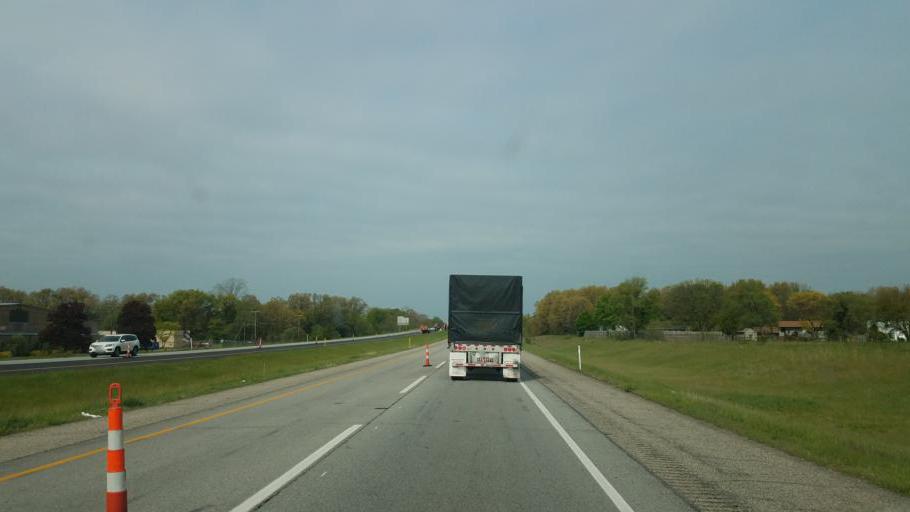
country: US
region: Indiana
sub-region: Elkhart County
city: Simonton Lake
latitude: 41.7312
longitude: -85.9785
